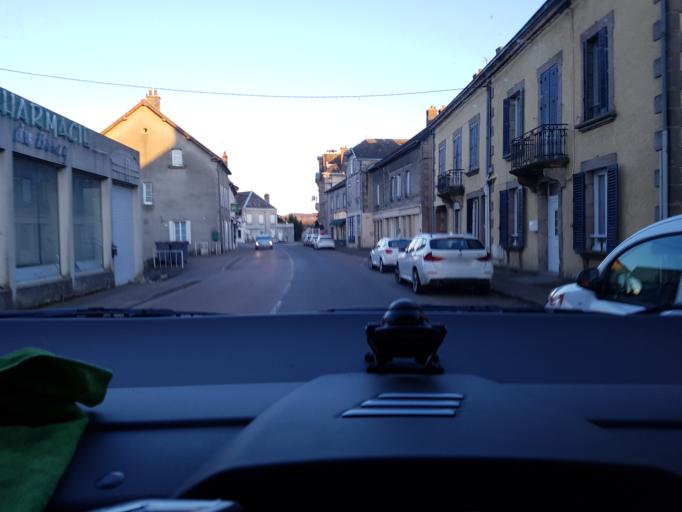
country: FR
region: Bourgogne
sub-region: Departement de Saone-et-Loire
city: Etang-sur-Arroux
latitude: 46.8670
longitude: 4.1834
